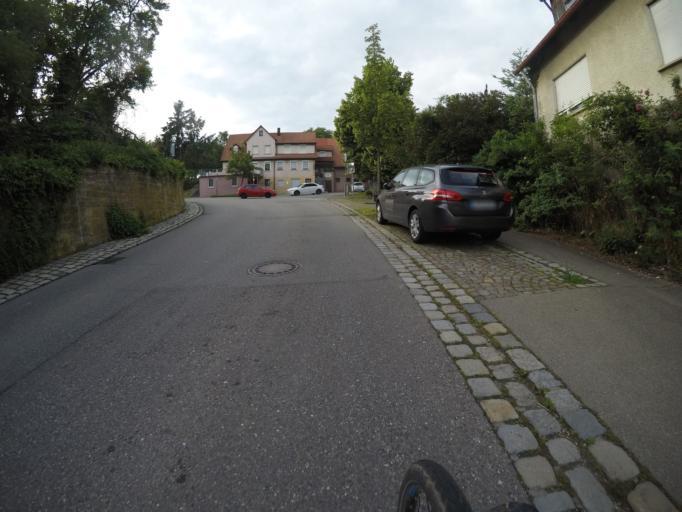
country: DE
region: Baden-Wuerttemberg
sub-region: Regierungsbezirk Stuttgart
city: Schlaitdorf
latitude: 48.6047
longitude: 9.2200
